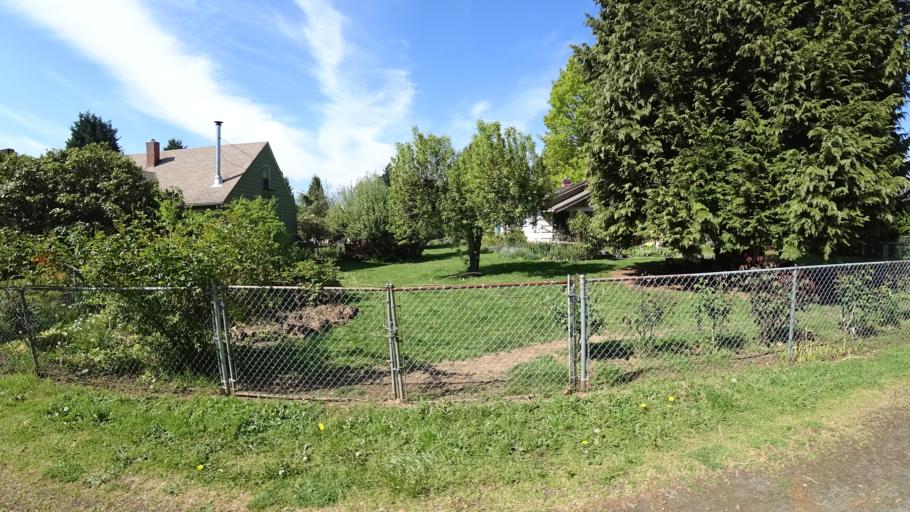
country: US
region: Oregon
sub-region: Clackamas County
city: Milwaukie
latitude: 45.4538
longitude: -122.6284
